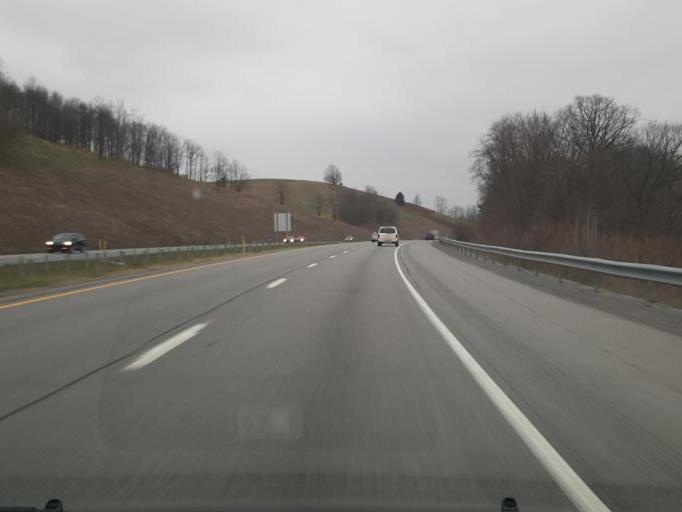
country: US
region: Pennsylvania
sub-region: Blair County
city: Duncansville
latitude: 40.4522
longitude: -78.4220
